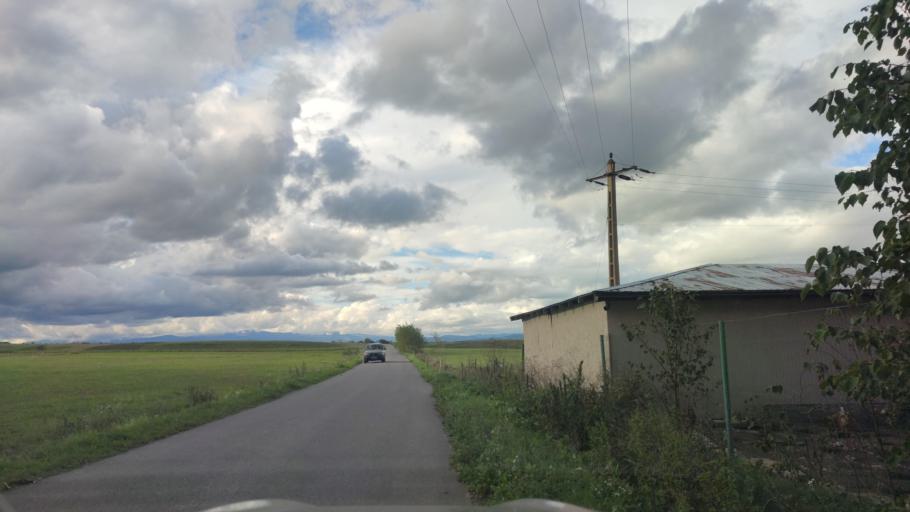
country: RO
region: Harghita
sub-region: Comuna Remetea
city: Remetea
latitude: 46.8113
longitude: 25.4362
